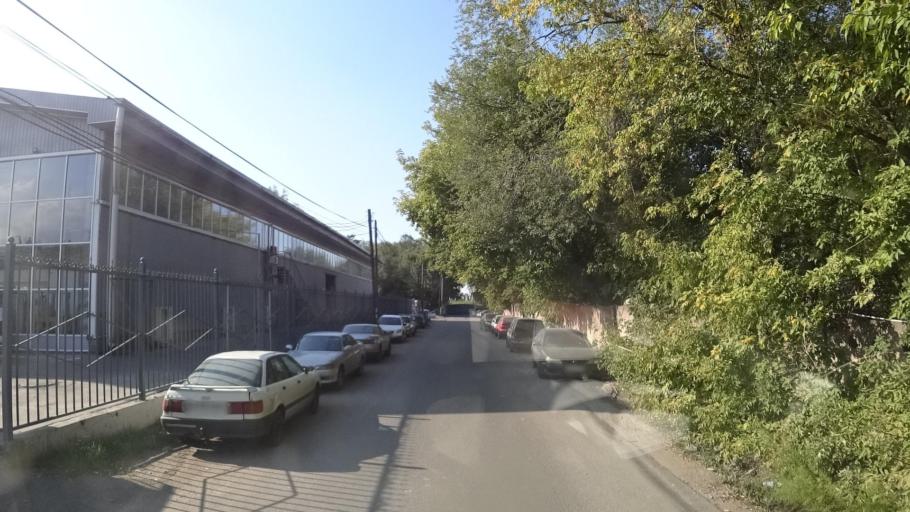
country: KZ
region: Almaty Qalasy
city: Almaty
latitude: 43.2887
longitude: 76.9227
